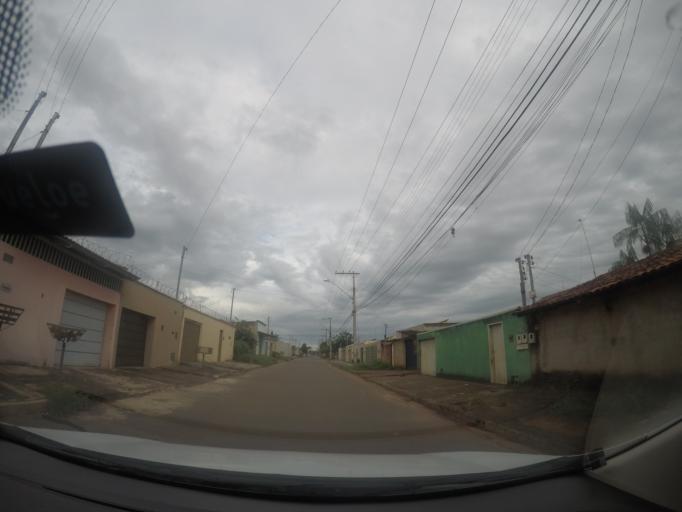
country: BR
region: Goias
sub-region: Goiania
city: Goiania
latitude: -16.5959
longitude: -49.3081
